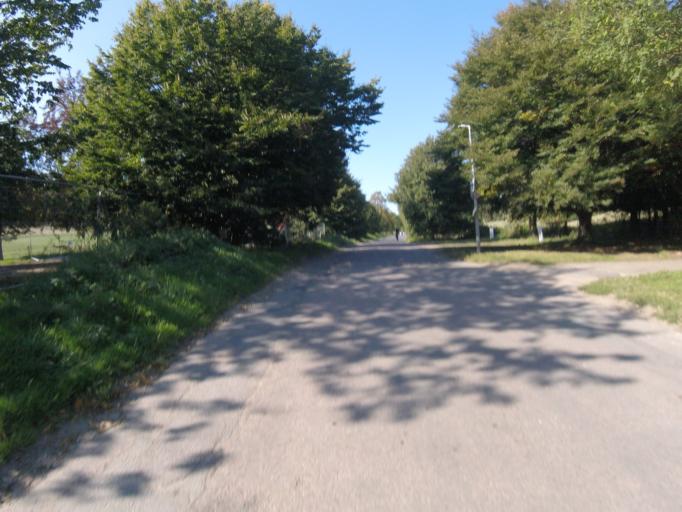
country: GB
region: England
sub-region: Brighton and Hove
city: Brighton
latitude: 50.8650
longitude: -0.0962
